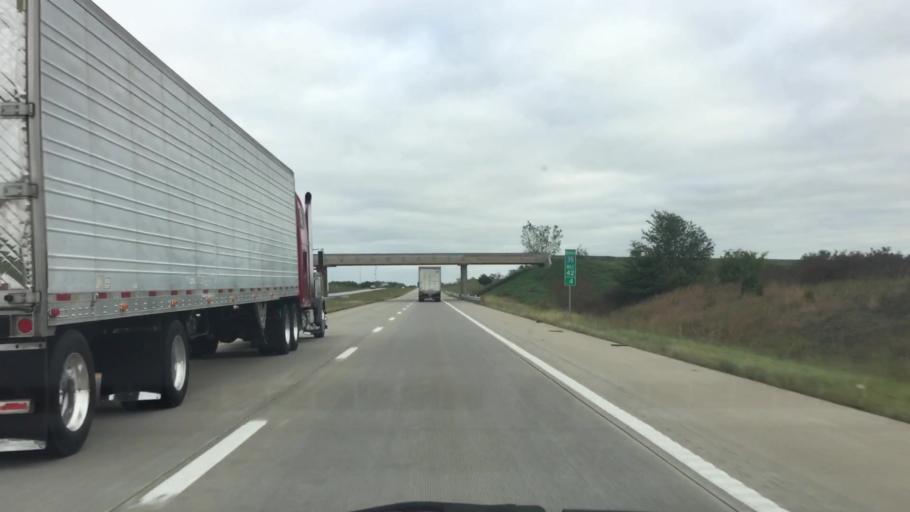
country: US
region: Missouri
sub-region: Clinton County
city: Lathrop
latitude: 39.5848
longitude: -94.2581
